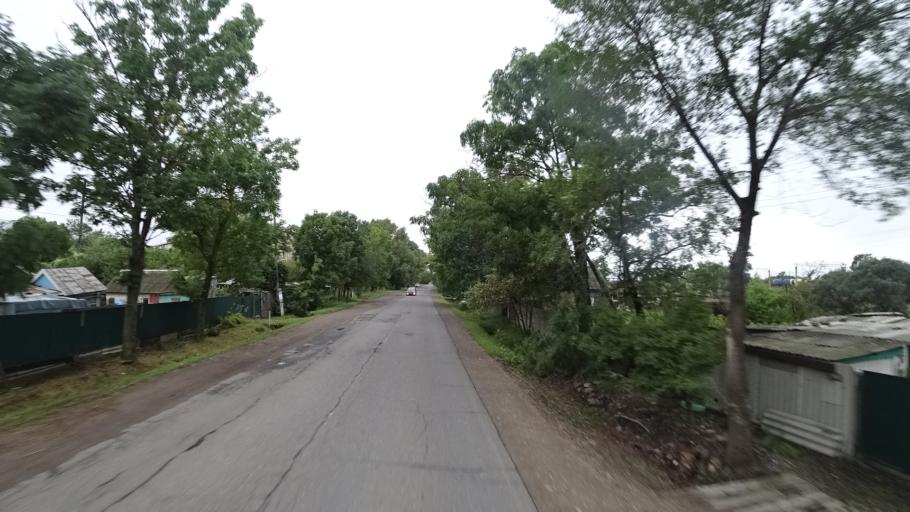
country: RU
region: Primorskiy
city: Chernigovka
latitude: 44.3372
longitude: 132.5325
